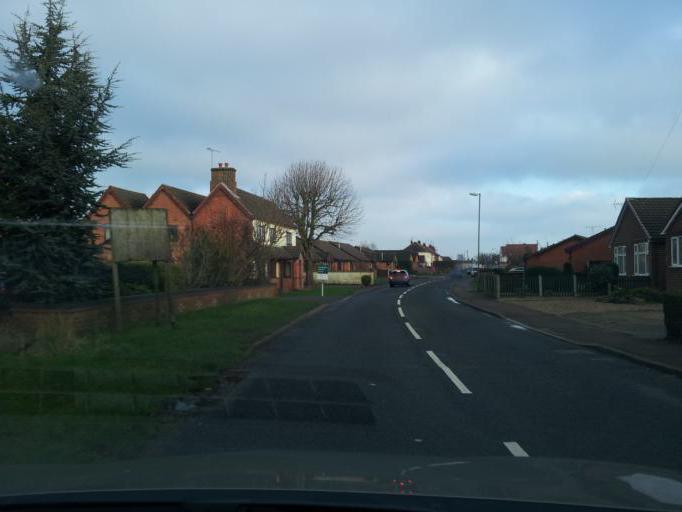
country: GB
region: England
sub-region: Staffordshire
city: Burton upon Trent
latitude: 52.8658
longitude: -1.6893
